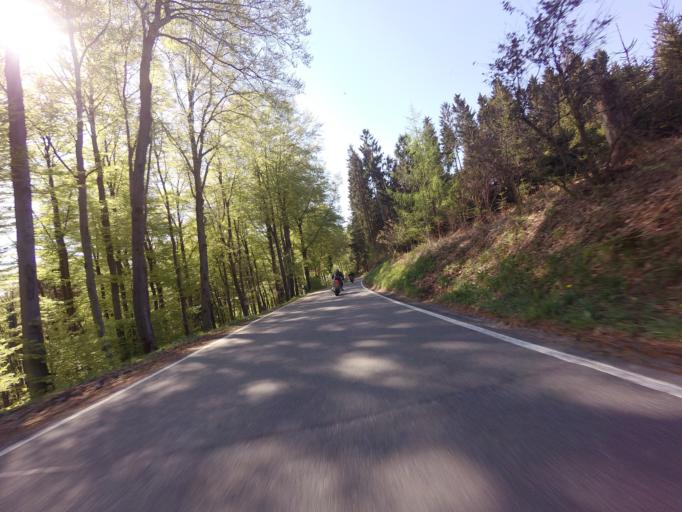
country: DE
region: North Rhine-Westphalia
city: Meinerzhagen
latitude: 51.1576
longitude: 7.6702
